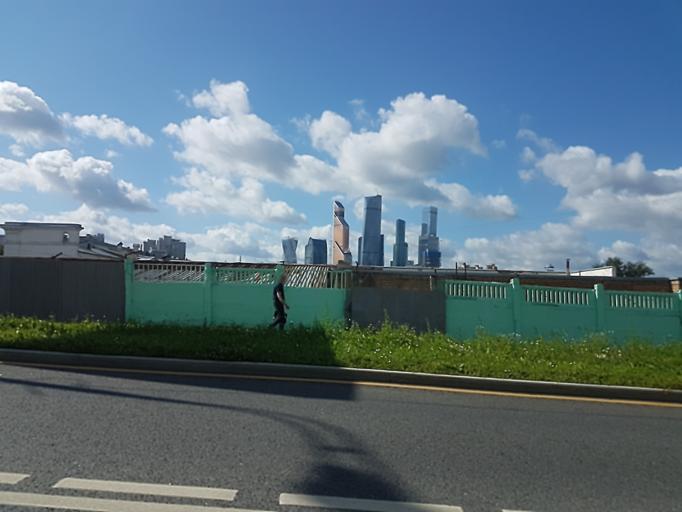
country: RU
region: Moskovskaya
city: Presnenskiy
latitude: 55.7653
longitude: 37.5446
